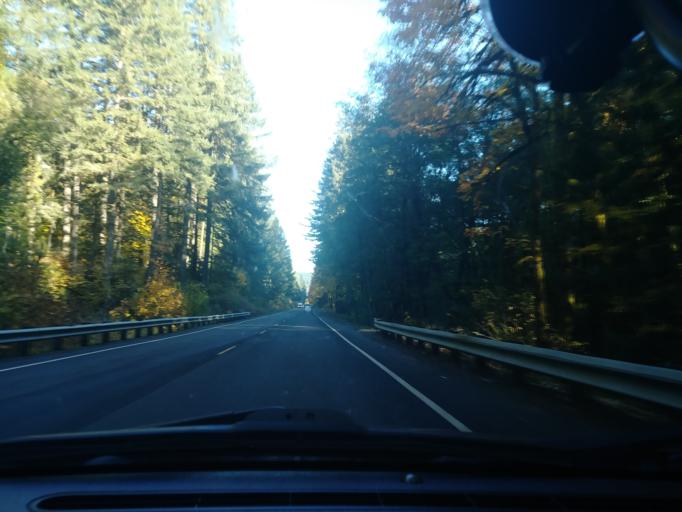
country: US
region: Oregon
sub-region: Washington County
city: Banks
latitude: 45.6530
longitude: -123.2927
